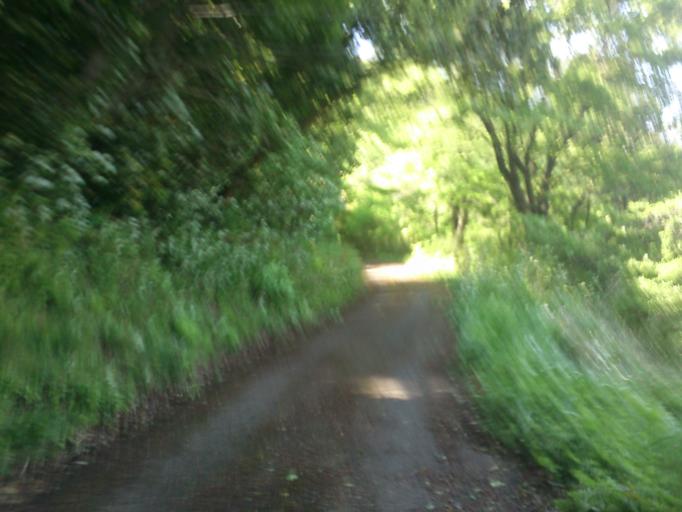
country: JP
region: Kyoto
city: Miyazu
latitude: 35.7129
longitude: 135.1442
